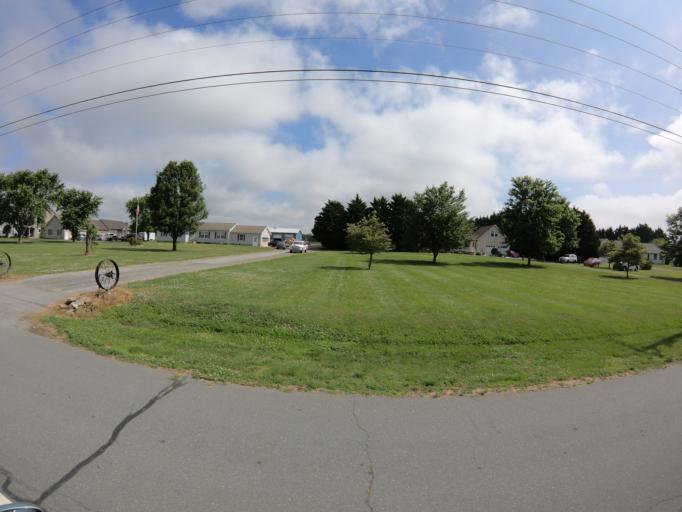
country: US
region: Delaware
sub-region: Kent County
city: Riverview
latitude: 39.0102
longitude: -75.4844
